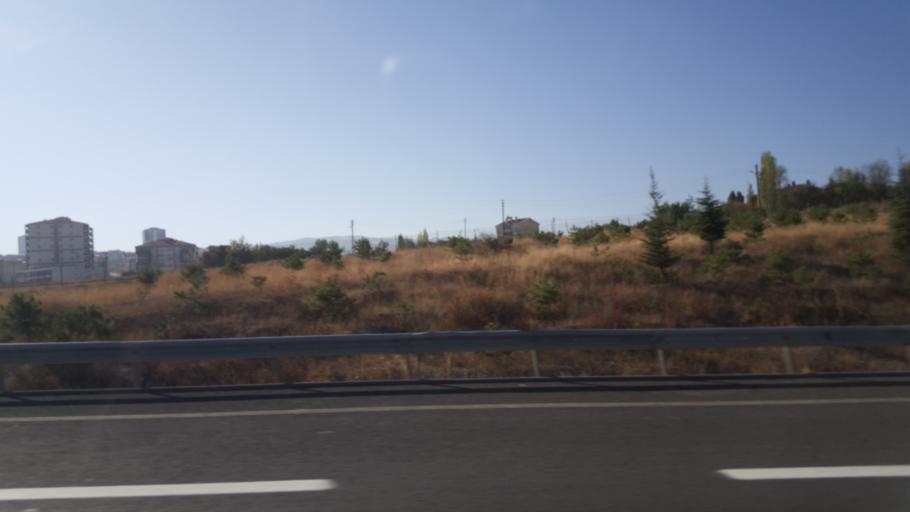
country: TR
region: Ankara
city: Mamak
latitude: 39.9024
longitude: 32.9745
